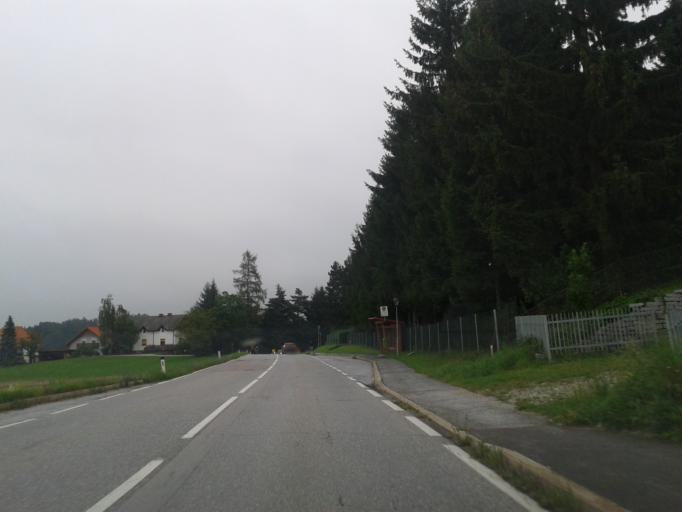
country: AT
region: Styria
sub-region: Politischer Bezirk Graz-Umgebung
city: Eggersdorf bei Graz
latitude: 47.1018
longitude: 15.5486
